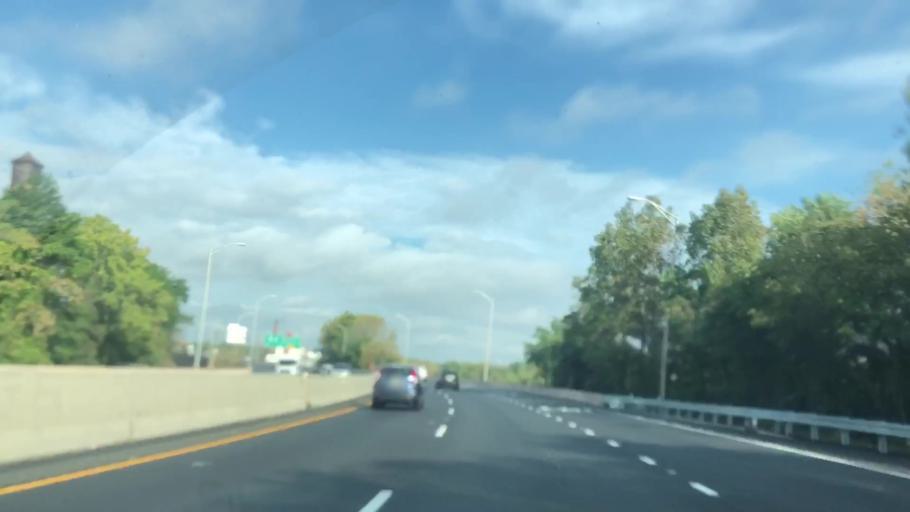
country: US
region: New Jersey
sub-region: Bergen County
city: Garfield
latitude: 40.8746
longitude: -74.1169
